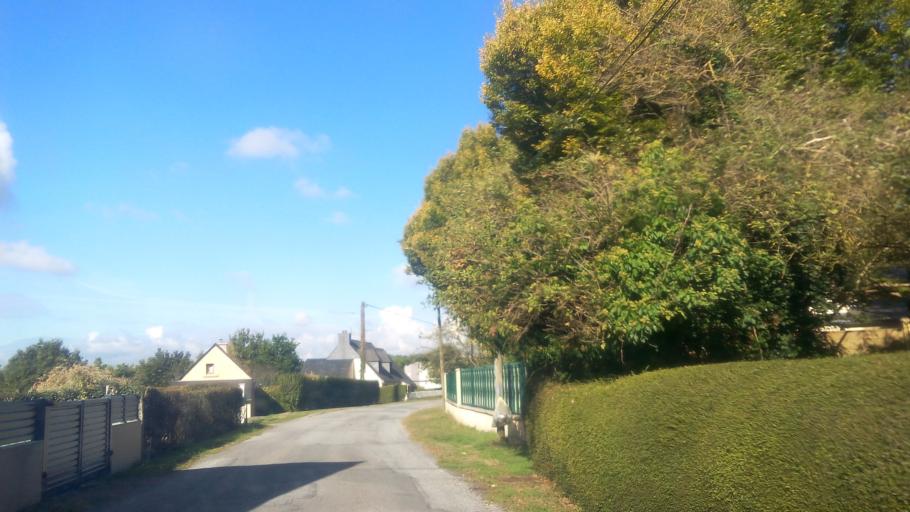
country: FR
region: Brittany
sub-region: Departement du Morbihan
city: Saint-Perreux
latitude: 47.6734
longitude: -2.0877
